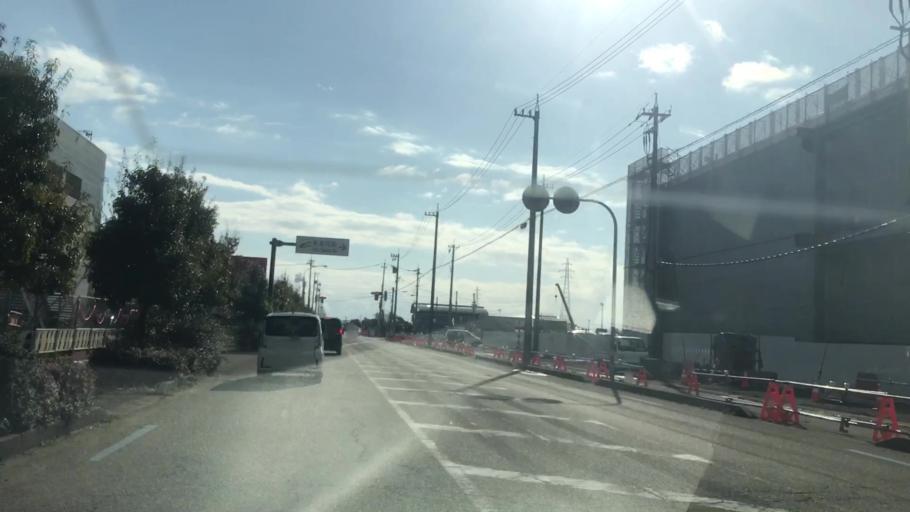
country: JP
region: Toyama
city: Takaoka
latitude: 36.7245
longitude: 137.0148
